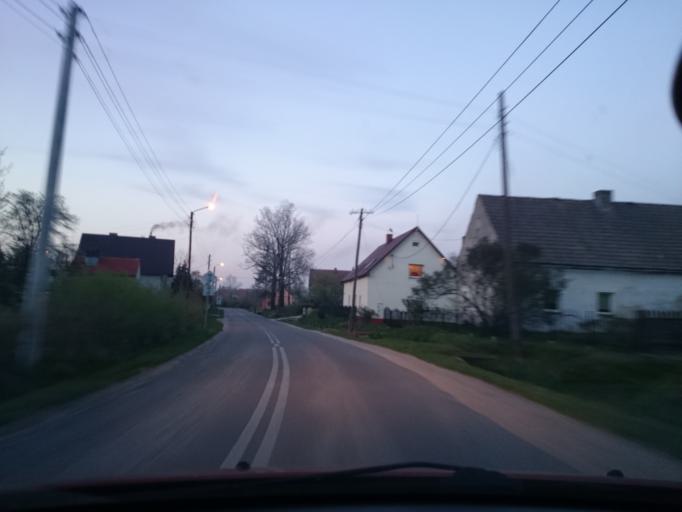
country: PL
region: Lower Silesian Voivodeship
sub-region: Powiat zabkowicki
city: Budzow
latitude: 50.5745
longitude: 16.6810
